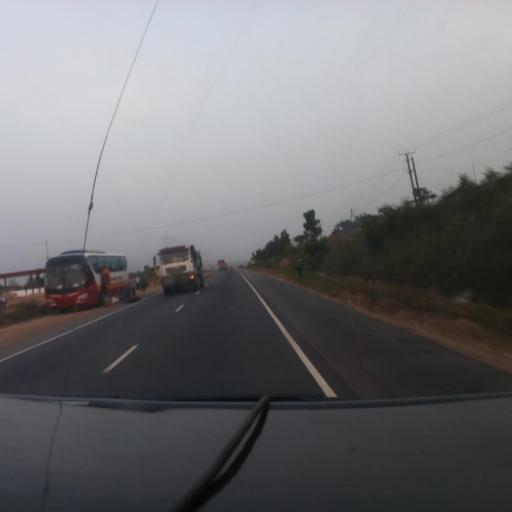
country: GH
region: Eastern
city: Nsawam
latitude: 5.8787
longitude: -0.3733
